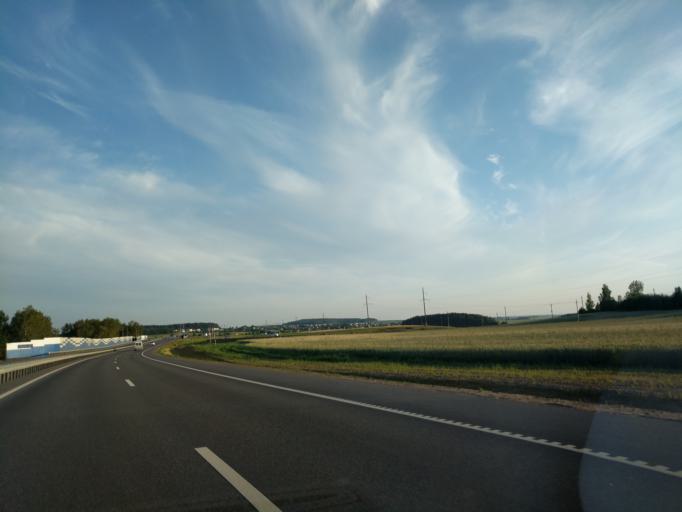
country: BY
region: Minsk
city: Bal'shavik
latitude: 54.0459
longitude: 27.5639
